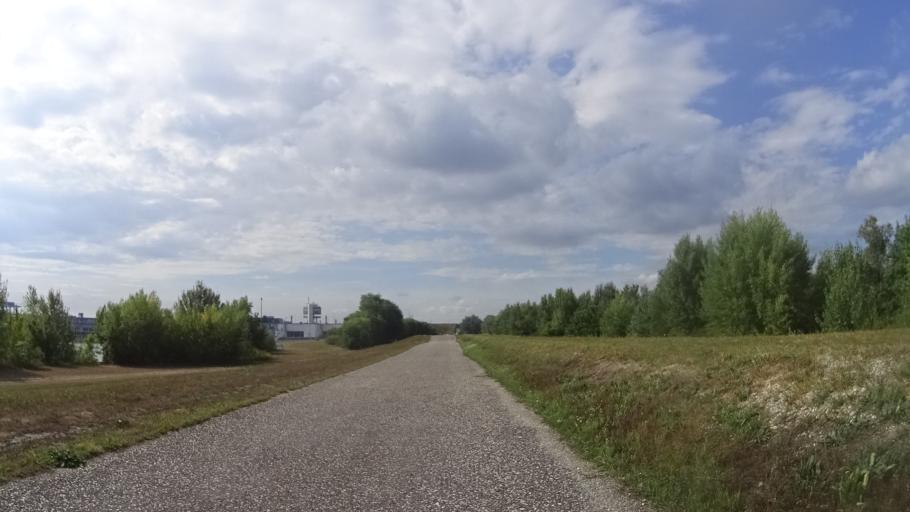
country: SK
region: Trnavsky
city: Gabcikovo
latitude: 47.8779
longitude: 17.5493
